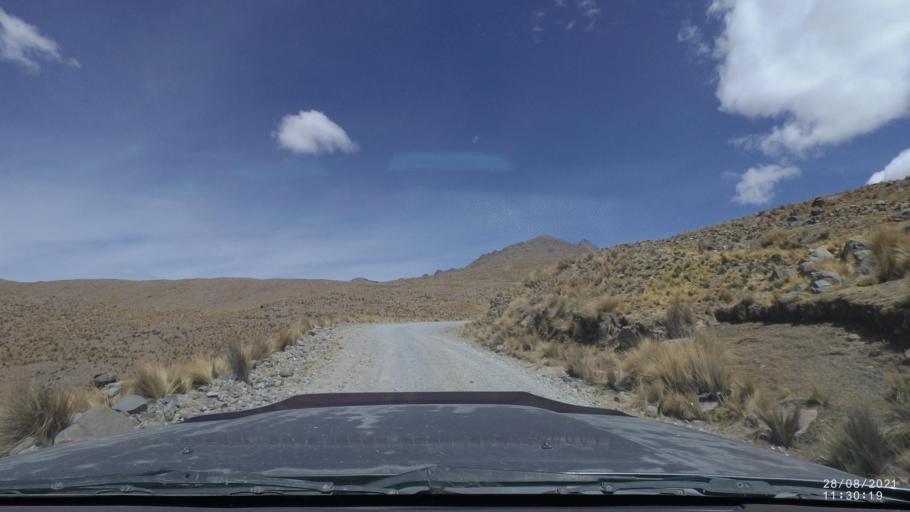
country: BO
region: Cochabamba
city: Sipe Sipe
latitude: -17.1808
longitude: -66.3623
